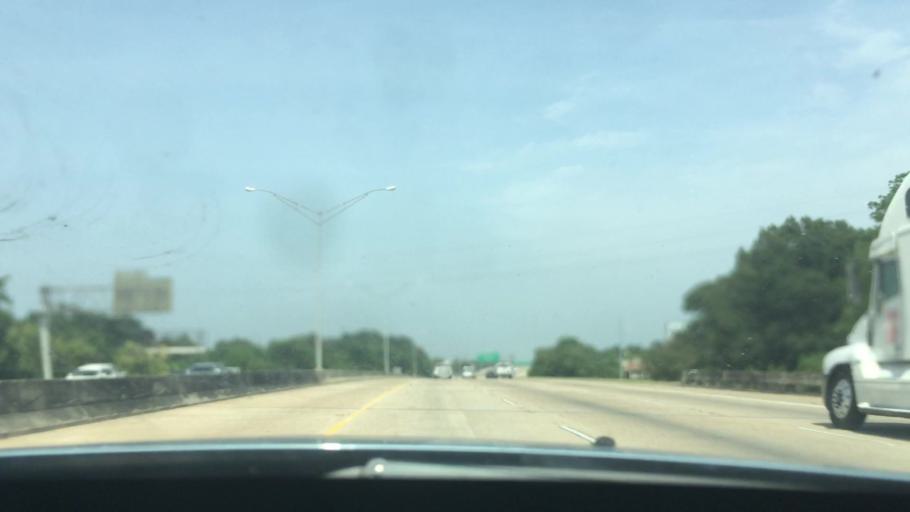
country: US
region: Louisiana
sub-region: East Baton Rouge Parish
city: Westminster
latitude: 30.4273
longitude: -91.0668
